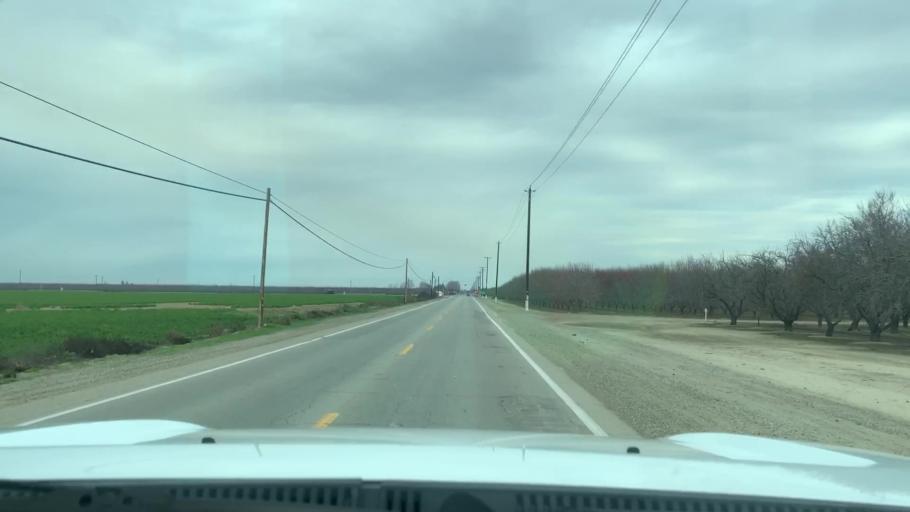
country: US
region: California
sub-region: Kern County
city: Rosedale
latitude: 35.3936
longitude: -119.2520
